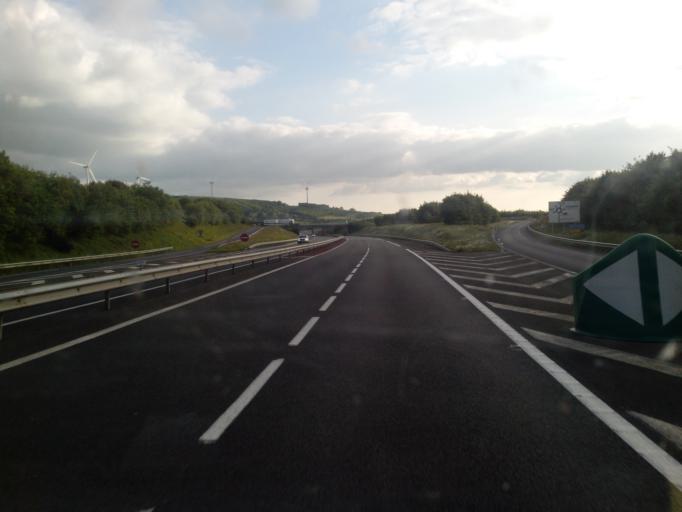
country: FR
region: Lower Normandy
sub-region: Departement de la Manche
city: Saint-Amand
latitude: 48.9814
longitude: -0.9475
